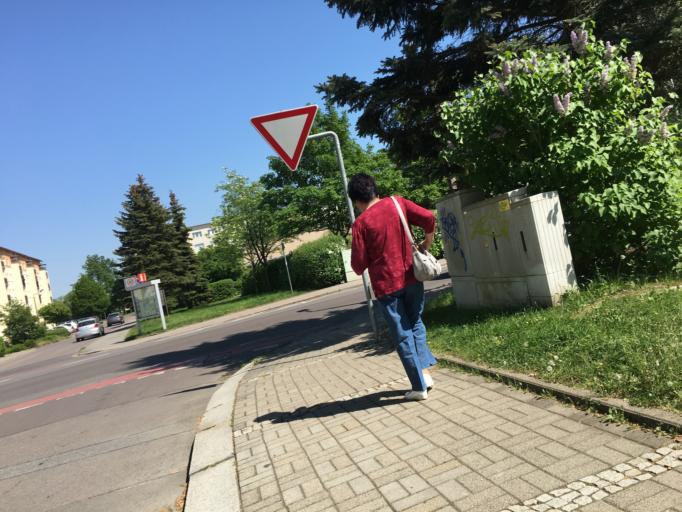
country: DE
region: Saxony
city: Borna
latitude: 51.1189
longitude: 12.4939
